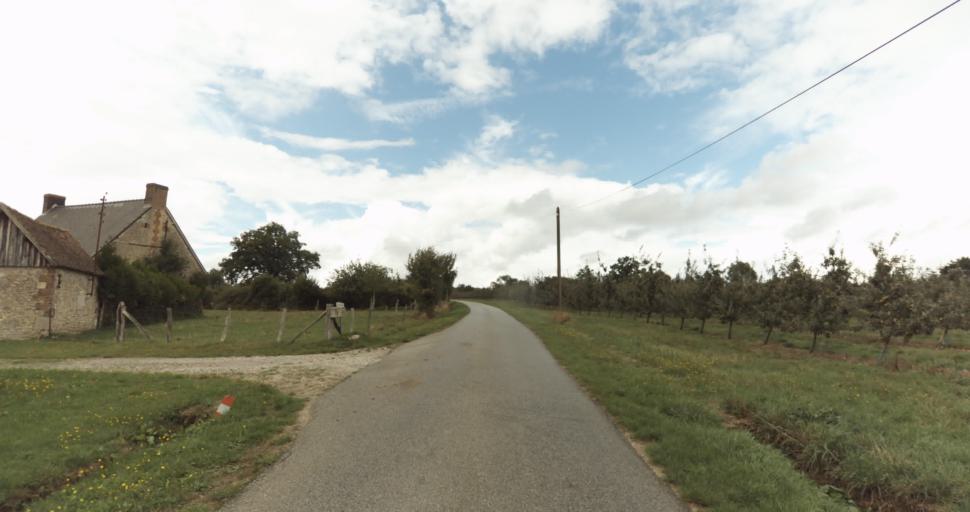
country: FR
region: Lower Normandy
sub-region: Departement de l'Orne
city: Sainte-Gauburge-Sainte-Colombe
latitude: 48.7153
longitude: 0.3953
